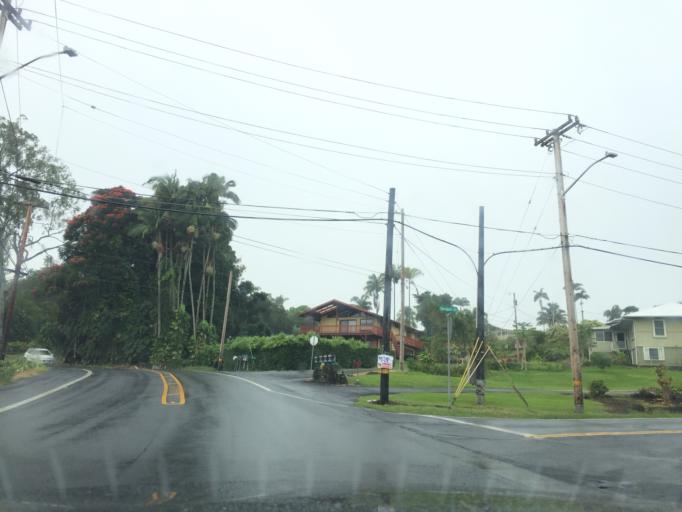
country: US
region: Hawaii
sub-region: Hawaii County
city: Hilo
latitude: 19.7029
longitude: -155.1131
